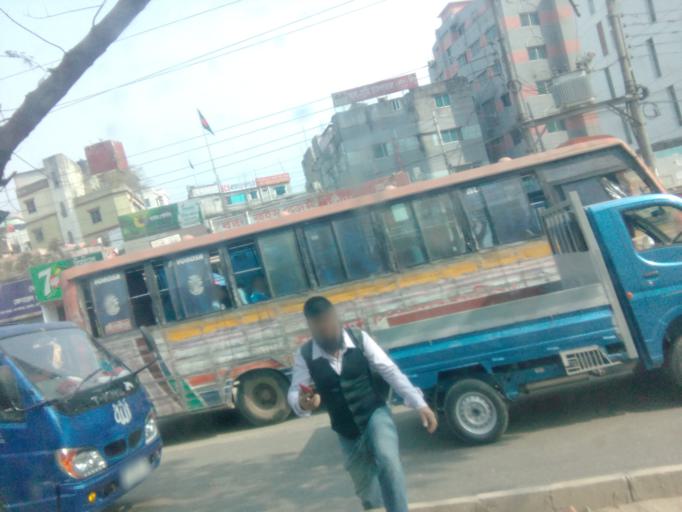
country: BD
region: Dhaka
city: Paltan
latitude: 23.7803
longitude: 90.4257
